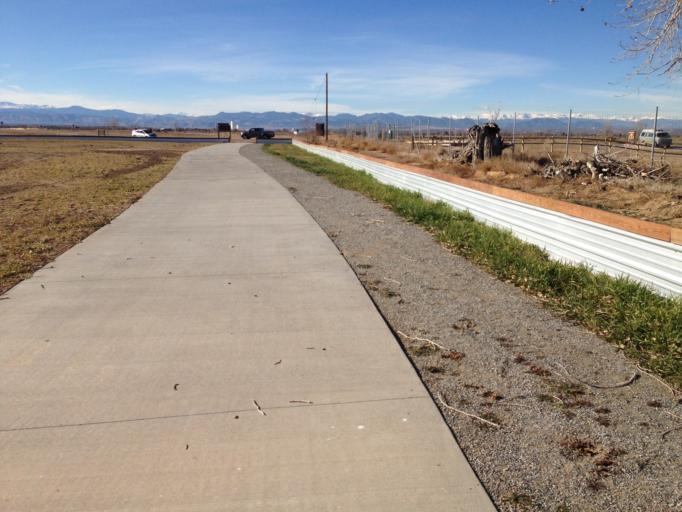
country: US
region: Colorado
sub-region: Adams County
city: Derby
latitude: 39.8128
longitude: -104.8834
